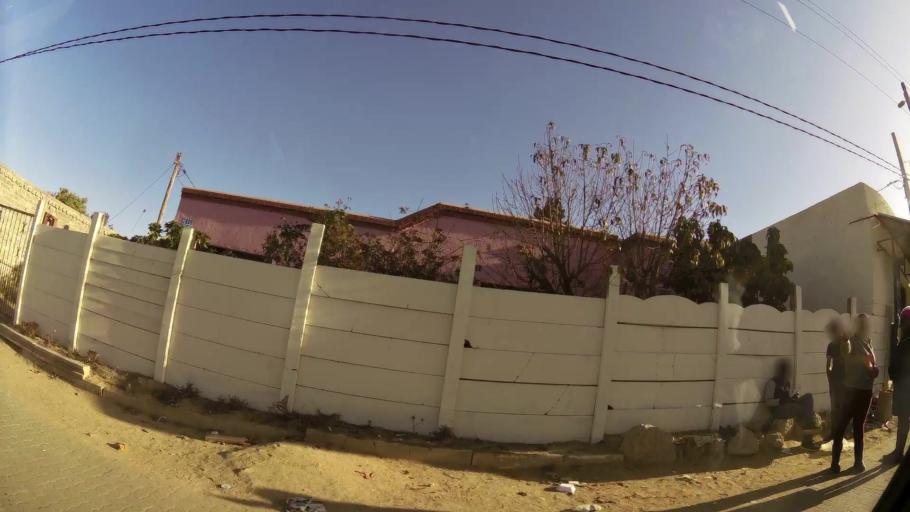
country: ZA
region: Gauteng
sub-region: City of Johannesburg Metropolitan Municipality
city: Diepsloot
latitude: -25.9297
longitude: 28.0069
